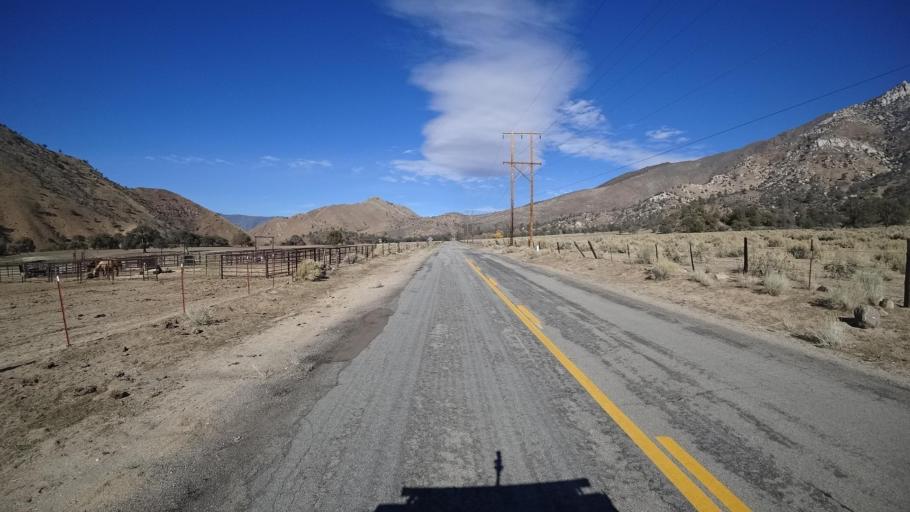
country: US
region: California
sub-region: Kern County
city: Bodfish
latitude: 35.5369
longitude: -118.5108
